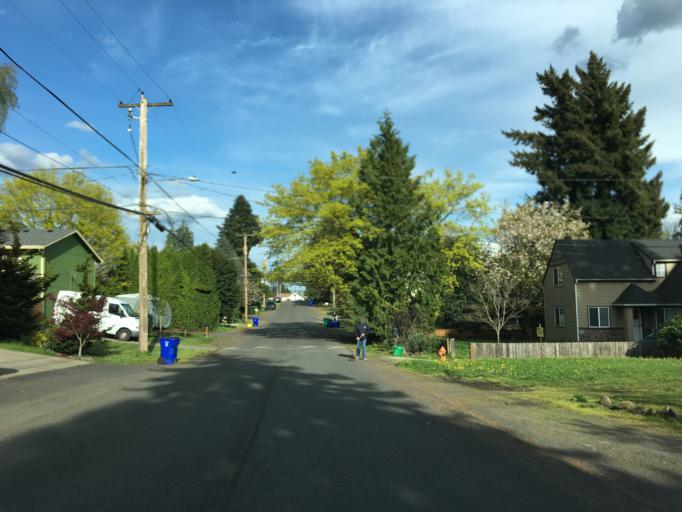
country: US
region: Oregon
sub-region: Multnomah County
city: Lents
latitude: 45.5435
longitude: -122.5561
